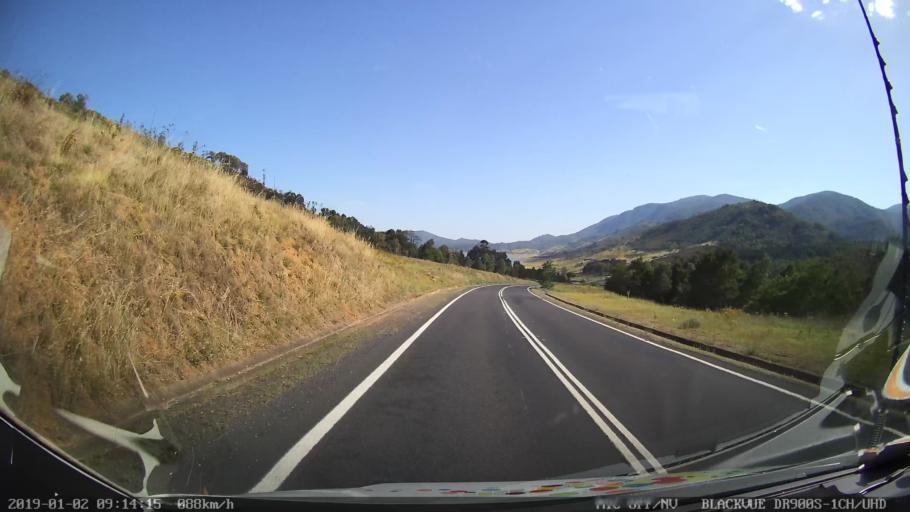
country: AU
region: New South Wales
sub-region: Tumut Shire
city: Tumut
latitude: -35.4796
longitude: 148.2729
